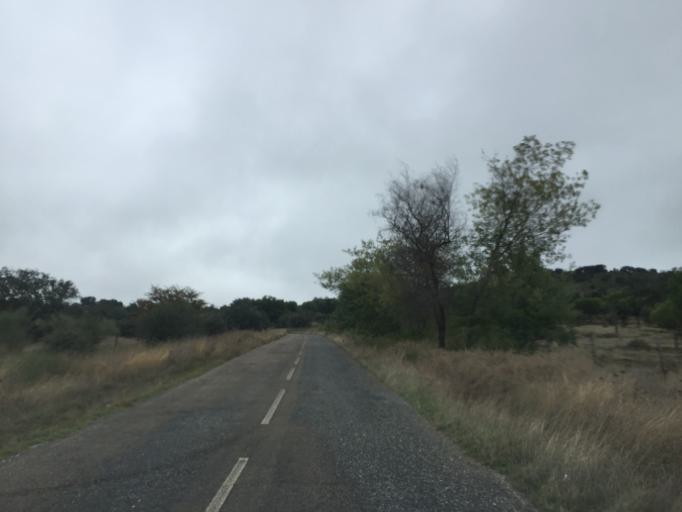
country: PT
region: Portalegre
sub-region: Alter do Chao
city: Alter do Chao
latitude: 39.2296
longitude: -7.6507
